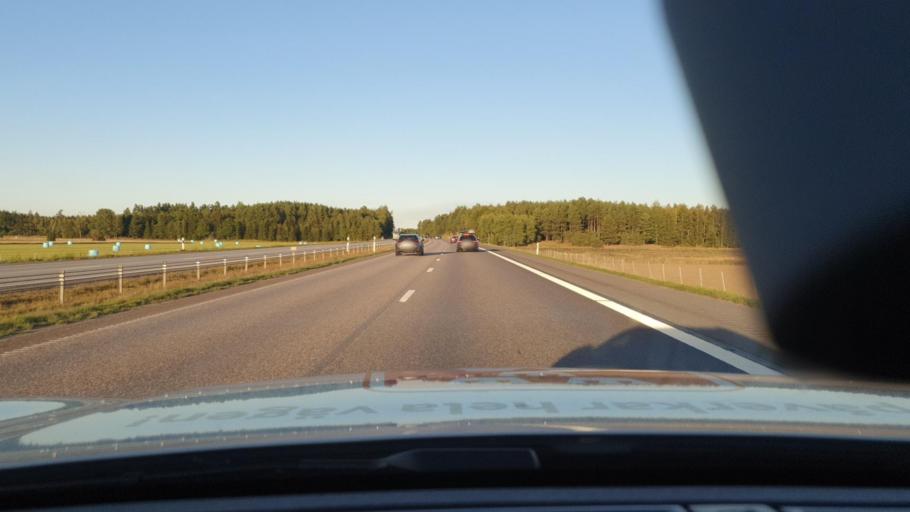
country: SE
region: OEstergoetland
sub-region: Linkopings Kommun
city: Linghem
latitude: 58.4511
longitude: 15.7517
